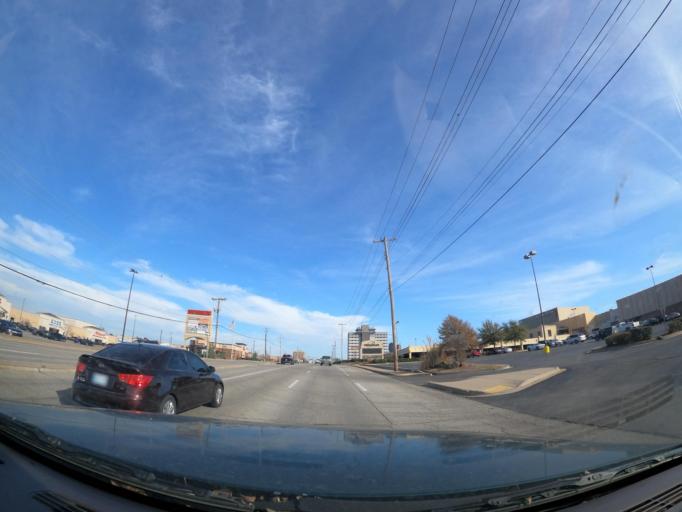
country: US
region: Oklahoma
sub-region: Tulsa County
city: Tulsa
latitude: 36.1044
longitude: -95.9211
